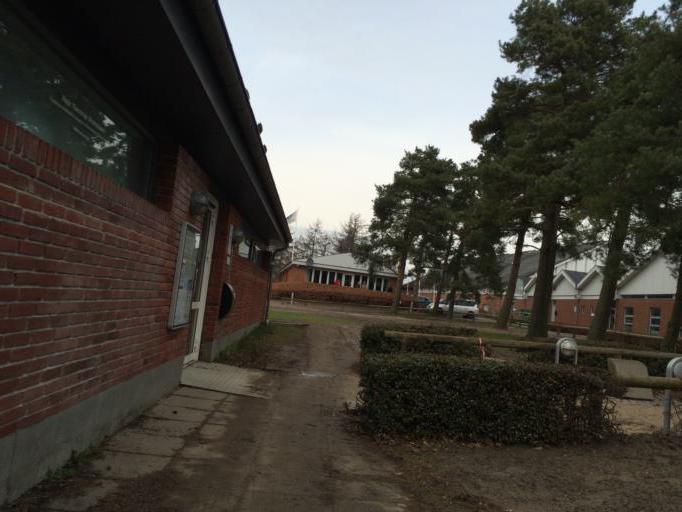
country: DK
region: Capital Region
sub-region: Hoje-Taastrup Kommune
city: Taastrup
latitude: 55.6510
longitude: 12.3170
